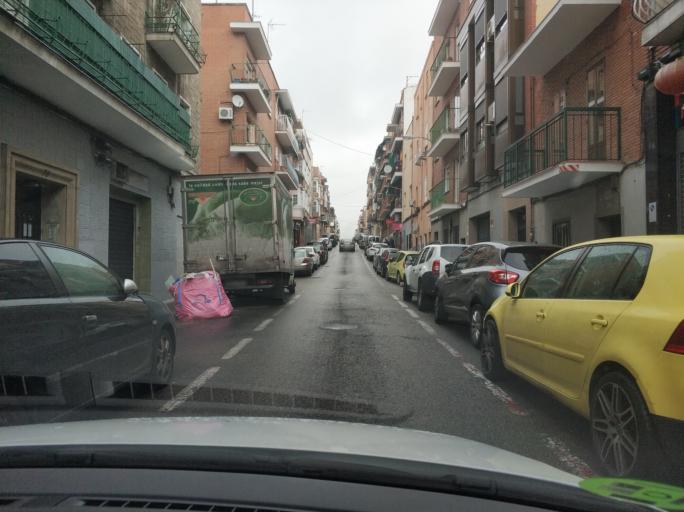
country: ES
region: Madrid
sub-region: Provincia de Madrid
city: Usera
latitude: 40.3836
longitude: -3.7054
